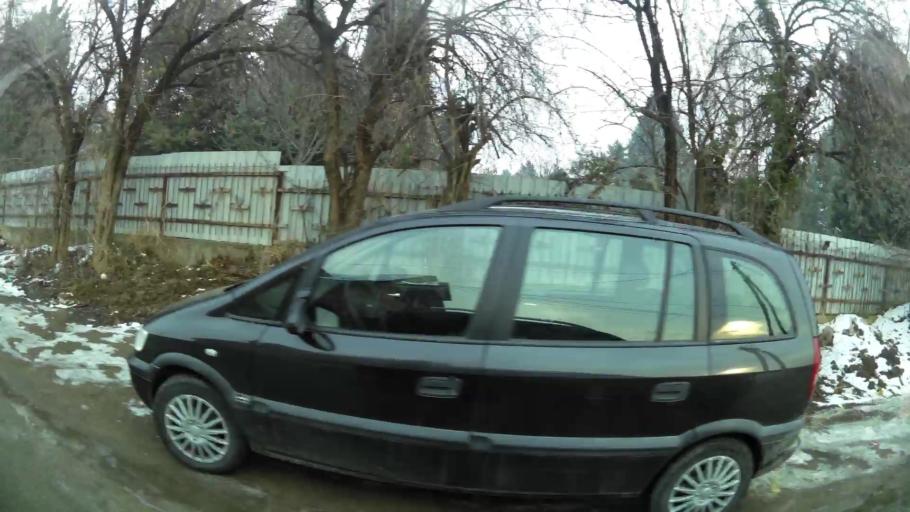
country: MK
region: Suto Orizari
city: Suto Orizare
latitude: 42.0337
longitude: 21.4332
